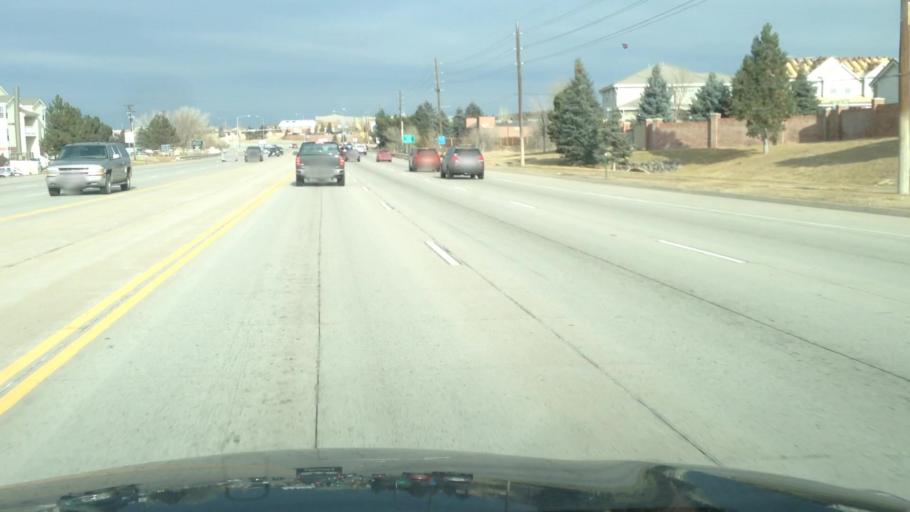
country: US
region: Colorado
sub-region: Arapahoe County
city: Dove Valley
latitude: 39.6076
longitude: -104.8091
